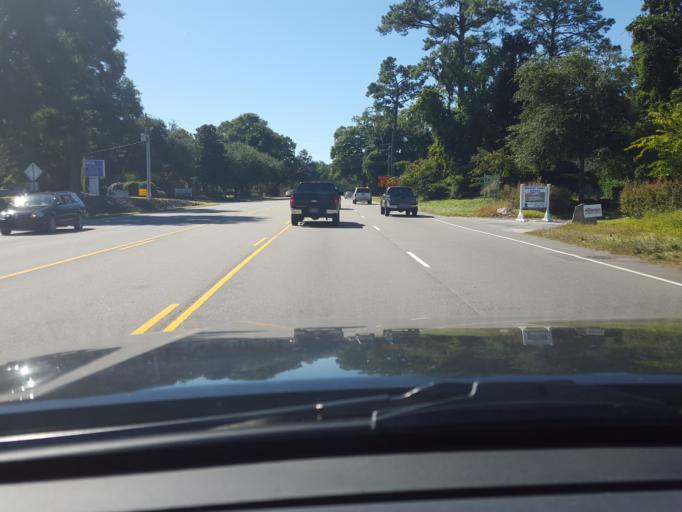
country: US
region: North Carolina
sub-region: New Hanover County
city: Seagate
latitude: 34.2130
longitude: -77.8349
